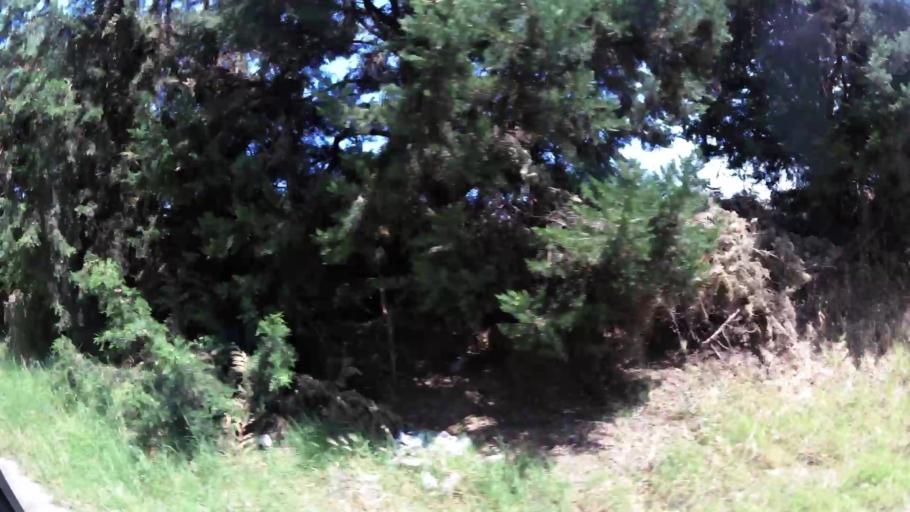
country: GR
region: Central Macedonia
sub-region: Nomos Thessalonikis
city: Neoi Epivates
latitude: 40.4978
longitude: 22.8955
